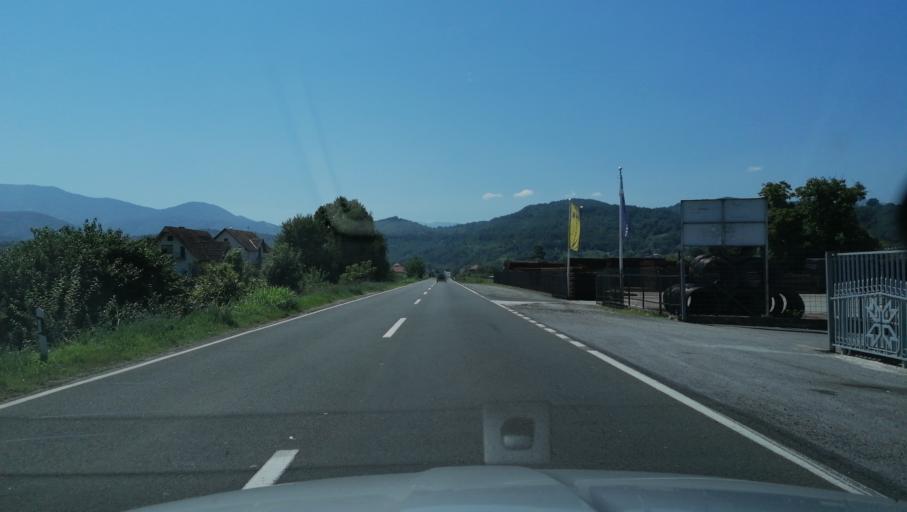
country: RS
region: Central Serbia
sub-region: Raski Okrug
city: Kraljevo
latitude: 43.6918
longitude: 20.5806
